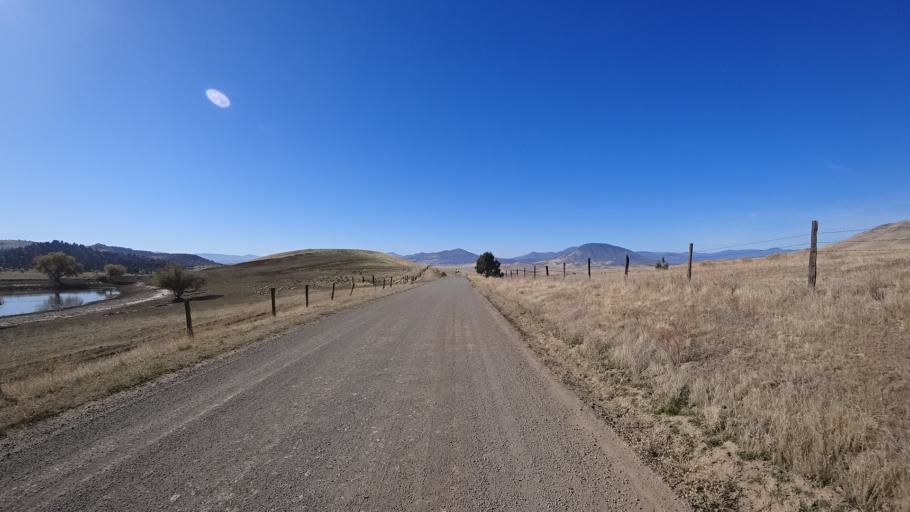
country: US
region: California
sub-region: Siskiyou County
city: Montague
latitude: 41.8153
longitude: -122.3655
